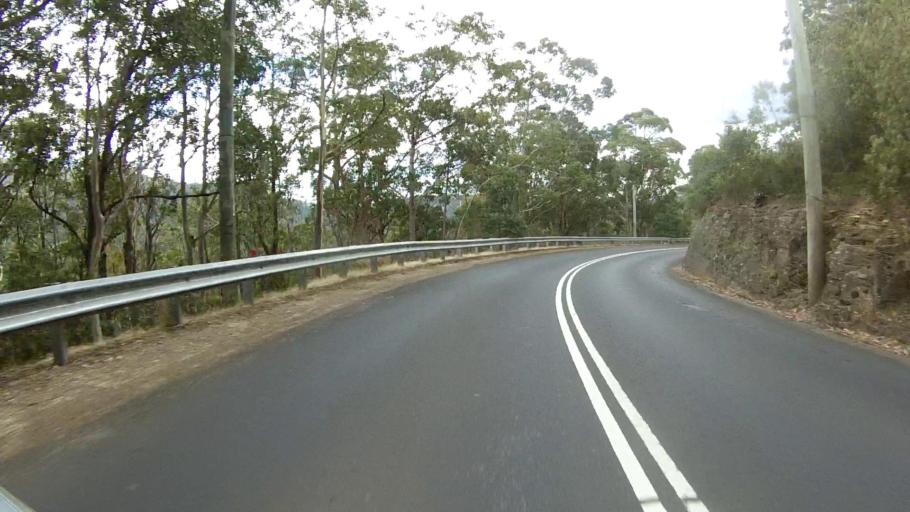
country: AU
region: Tasmania
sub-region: Hobart
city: Dynnyrne
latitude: -42.9072
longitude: 147.2744
